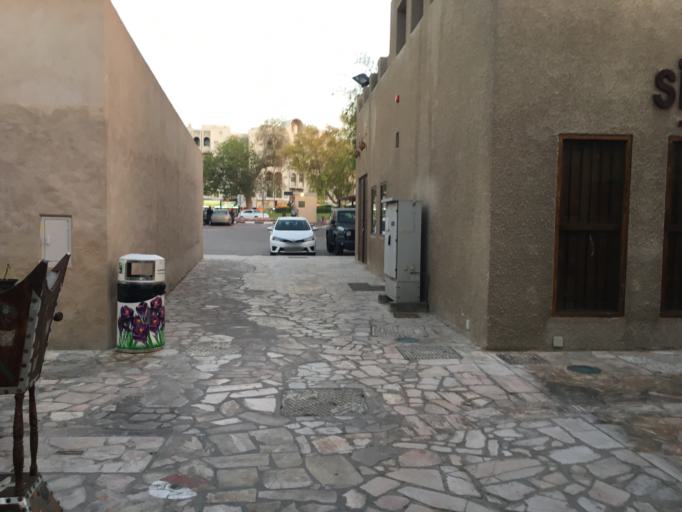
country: AE
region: Ash Shariqah
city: Sharjah
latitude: 25.2638
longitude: 55.3003
